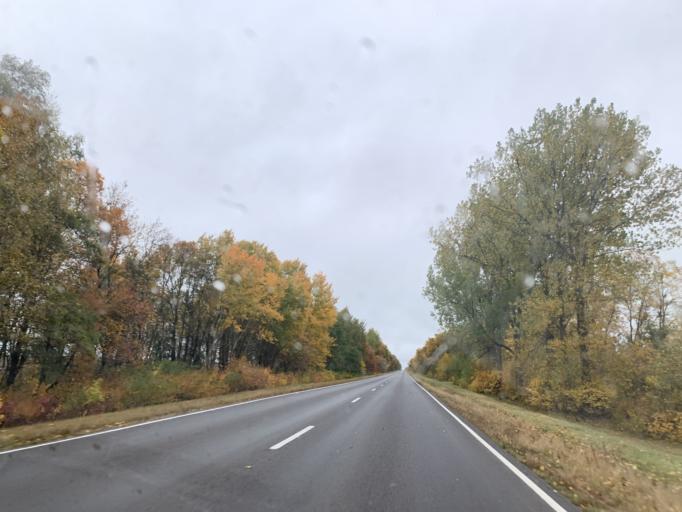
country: BY
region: Minsk
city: Haradzyeya
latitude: 53.4090
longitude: 26.6090
